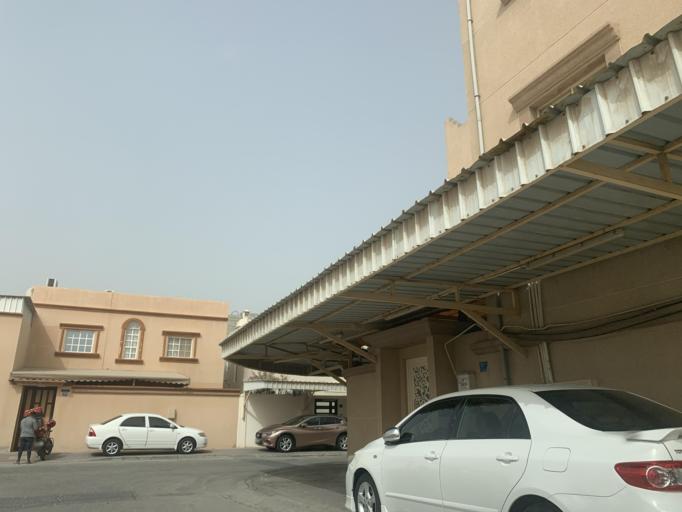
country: BH
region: Northern
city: Madinat `Isa
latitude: 26.1626
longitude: 50.5706
